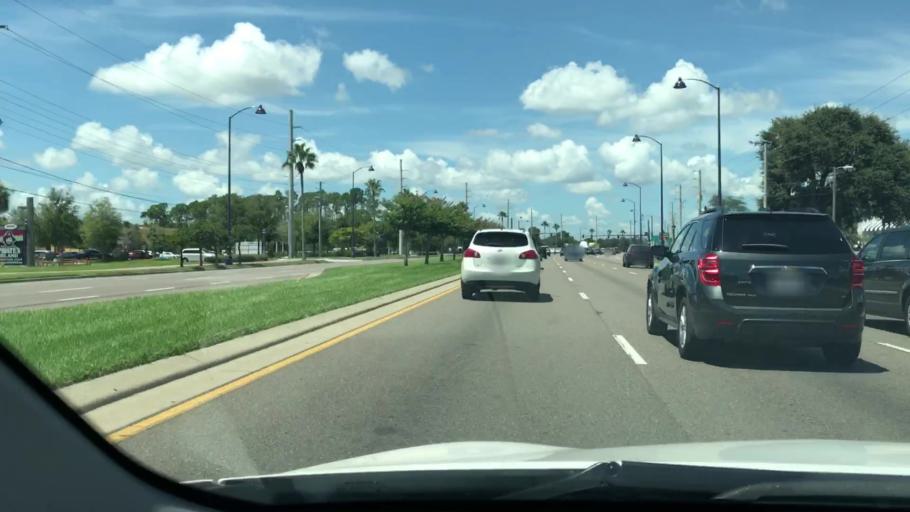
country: US
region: Florida
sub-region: Osceola County
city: Kissimmee
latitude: 28.3041
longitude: -81.4544
